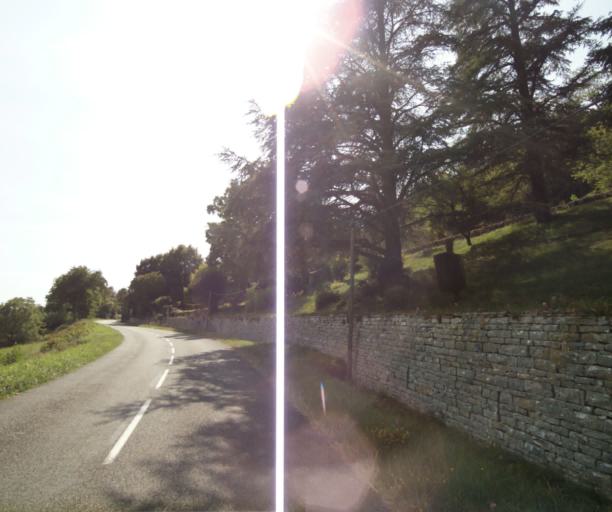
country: FR
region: Bourgogne
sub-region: Departement de Saone-et-Loire
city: Tournus
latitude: 46.5640
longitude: 4.8803
